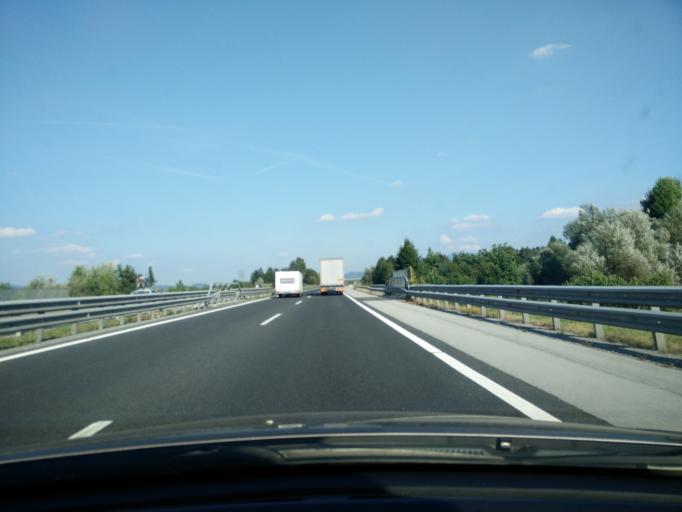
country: SI
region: Postojna
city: Postojna
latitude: 45.7637
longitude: 14.1115
